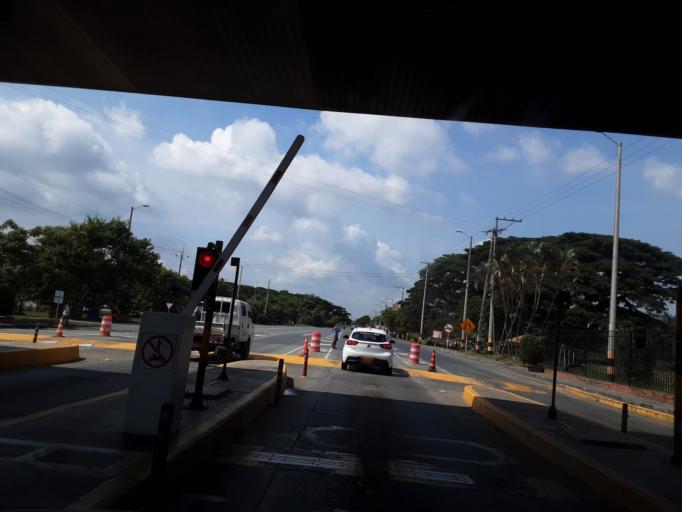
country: CO
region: Valle del Cauca
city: El Cerrito
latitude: 3.7131
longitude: -76.3195
